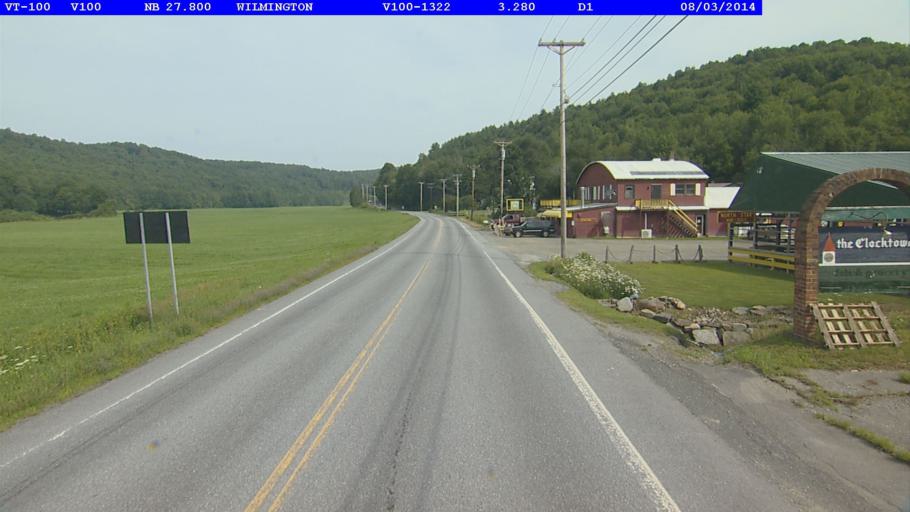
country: US
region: Vermont
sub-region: Windham County
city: Dover
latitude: 42.8770
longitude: -72.8622
